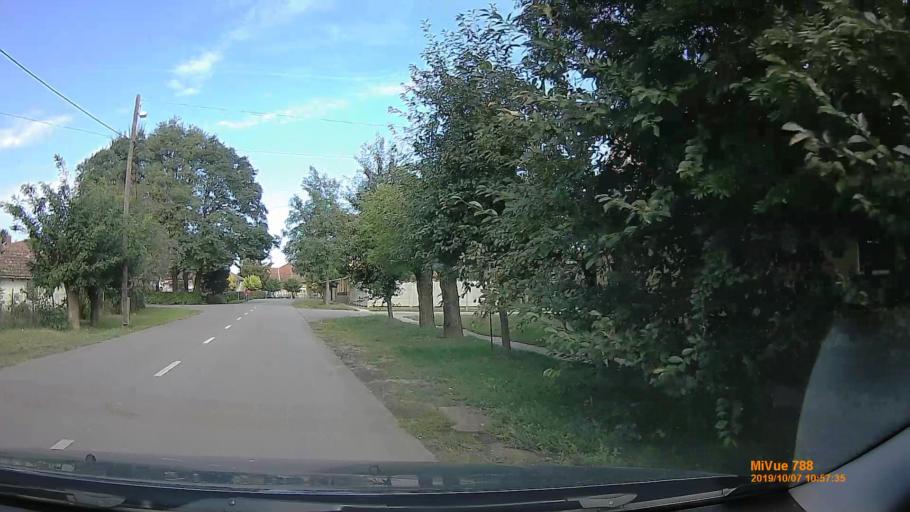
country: HU
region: Bekes
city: Kondoros
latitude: 46.7552
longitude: 20.7980
